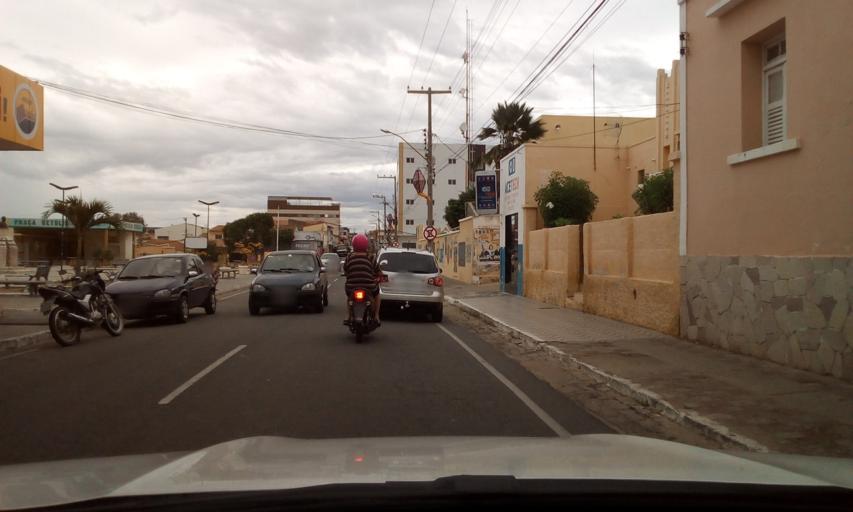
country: BR
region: Paraiba
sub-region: Picui
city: Picui
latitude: -6.5103
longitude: -36.3478
